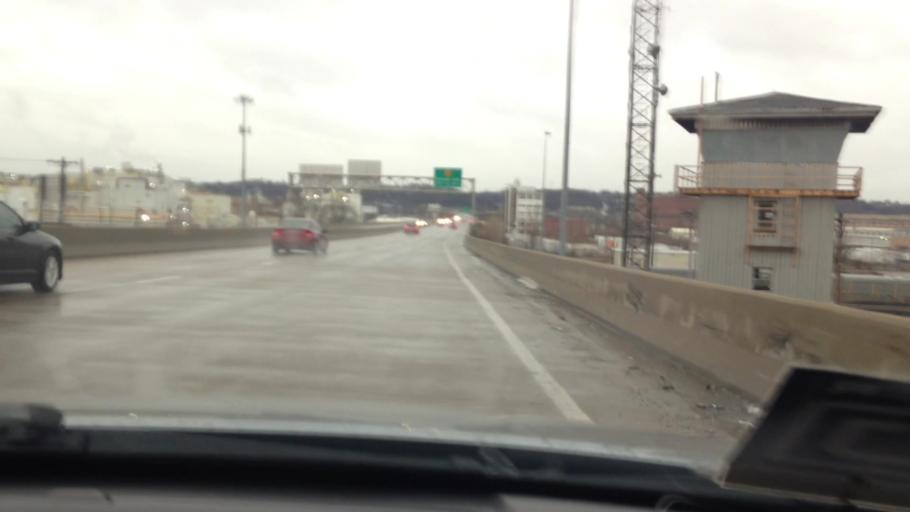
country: US
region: Kansas
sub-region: Wyandotte County
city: Kansas City
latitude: 39.0942
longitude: -94.6495
